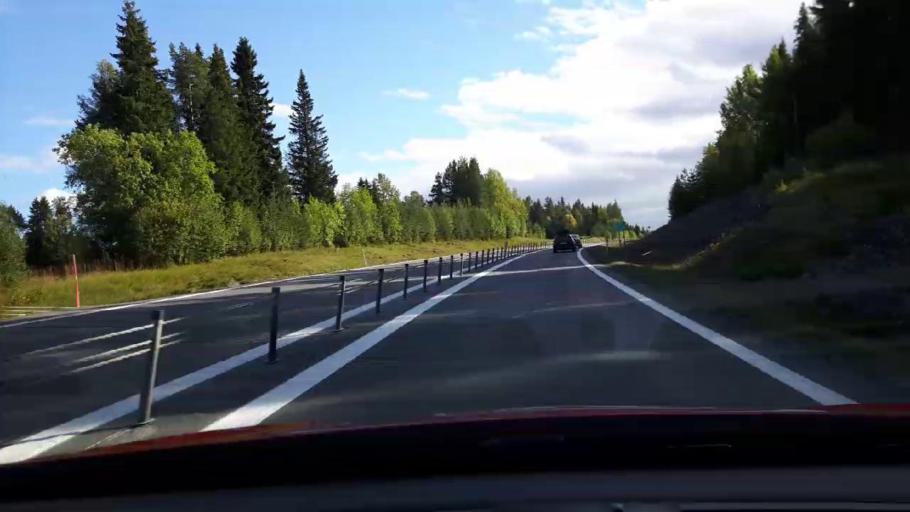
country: SE
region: Jaemtland
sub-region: OEstersunds Kommun
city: Brunflo
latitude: 63.1179
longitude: 14.7978
